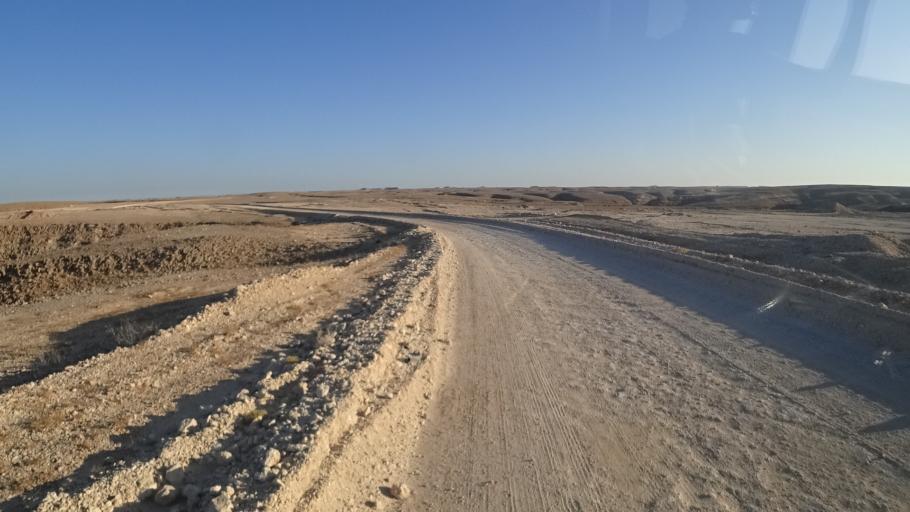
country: YE
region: Al Mahrah
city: Hawf
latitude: 17.1886
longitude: 53.3386
